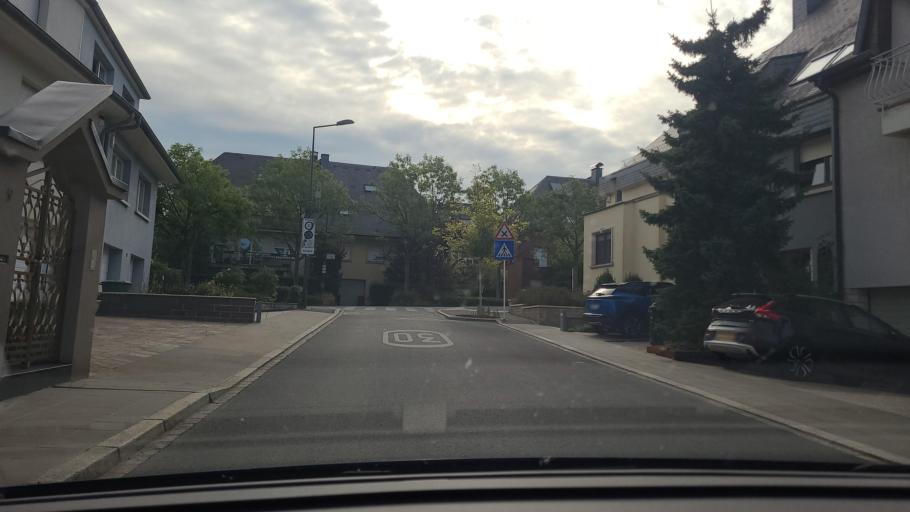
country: LU
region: Luxembourg
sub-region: Canton de Luxembourg
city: Luxembourg
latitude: 49.5941
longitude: 6.1478
